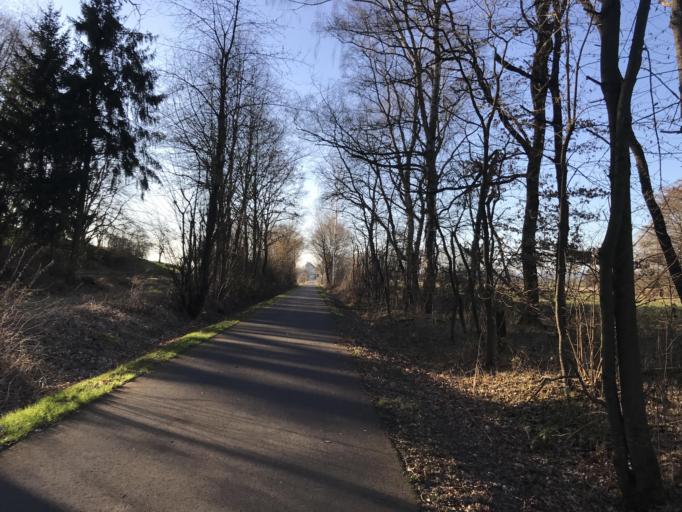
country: DE
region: Hesse
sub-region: Regierungsbezirk Kassel
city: Schrecksbach
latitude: 50.8746
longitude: 9.2785
